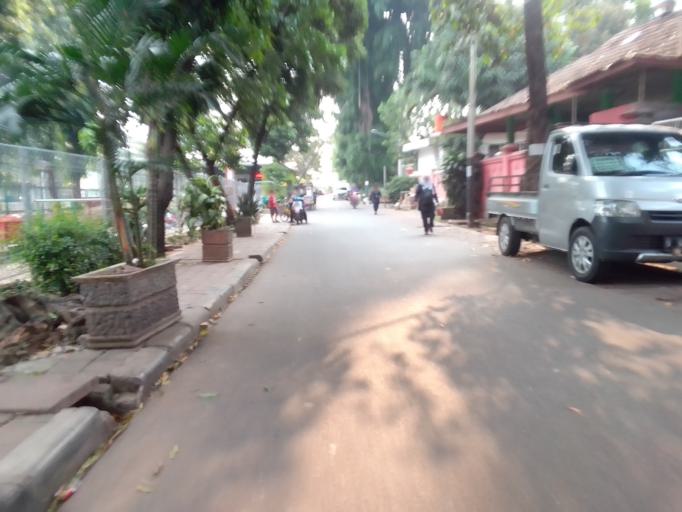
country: ID
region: Jakarta Raya
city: Jakarta
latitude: -6.2002
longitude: 106.8146
